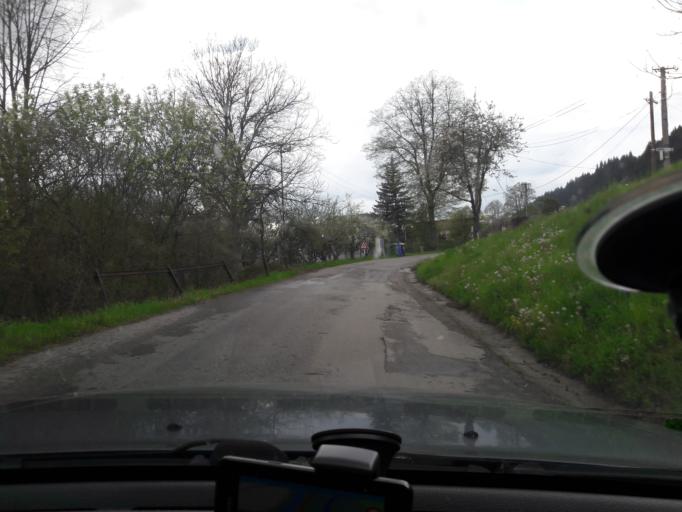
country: SK
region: Banskobystricky
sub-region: Okres Banska Bystrica
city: Brezno
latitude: 48.8130
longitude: 19.5902
